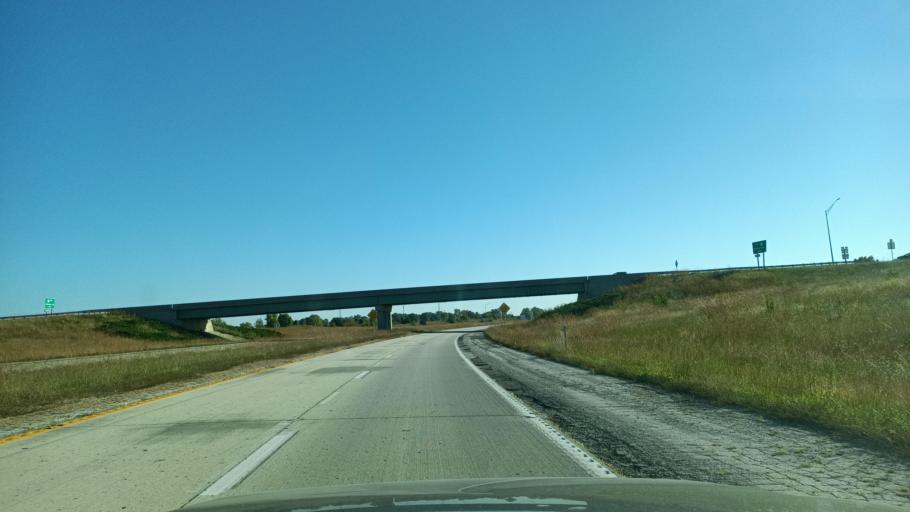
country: US
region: Missouri
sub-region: Audrain County
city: Mexico
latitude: 39.1165
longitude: -91.8930
